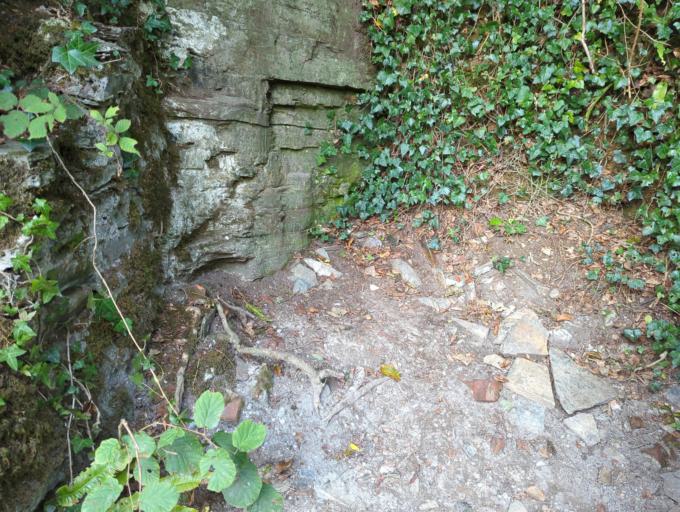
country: GB
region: England
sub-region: Cornwall
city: Tintagel
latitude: 50.6651
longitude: -4.7174
